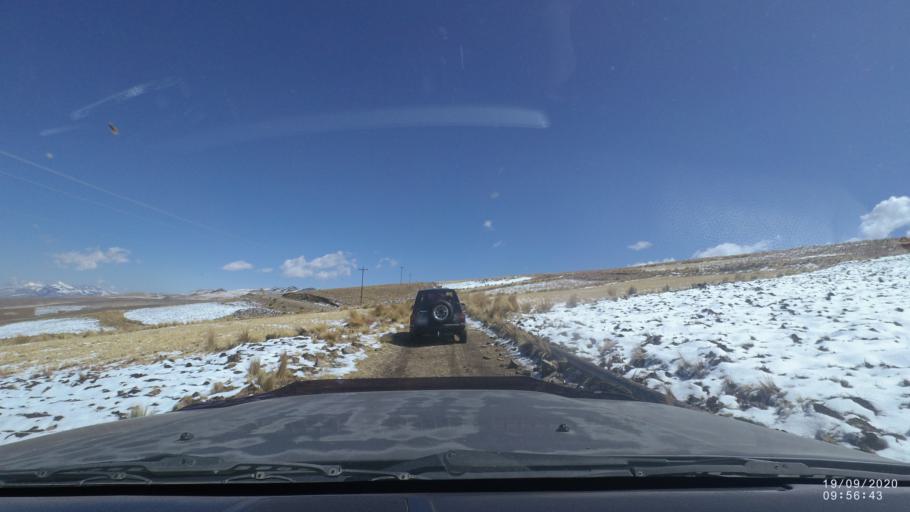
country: BO
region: Cochabamba
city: Cochabamba
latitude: -17.3125
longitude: -66.0829
